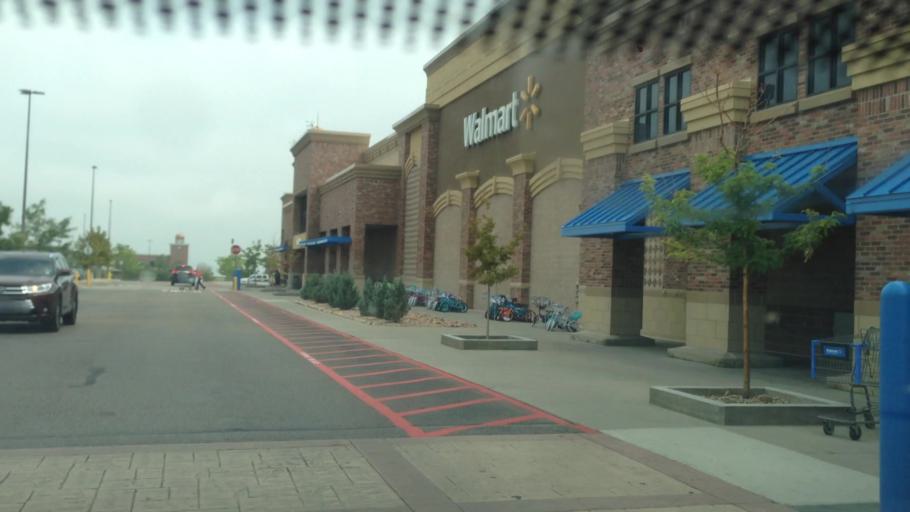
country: US
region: Colorado
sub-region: Douglas County
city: Parker
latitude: 39.6060
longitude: -104.7055
